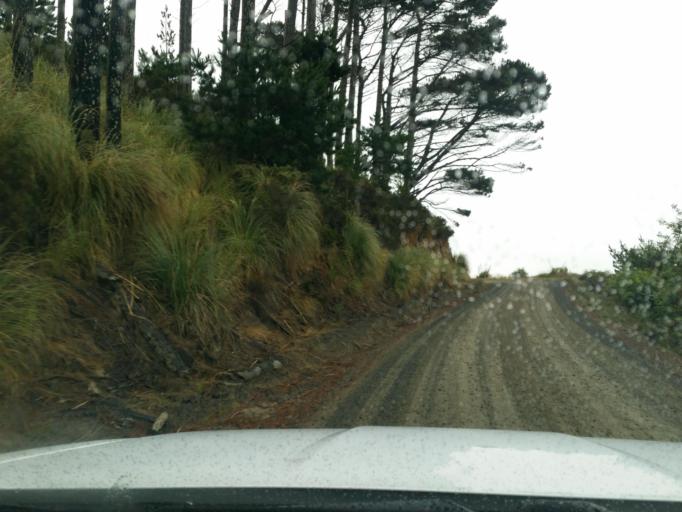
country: NZ
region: Northland
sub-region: Kaipara District
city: Dargaville
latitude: -36.0773
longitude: 173.8783
